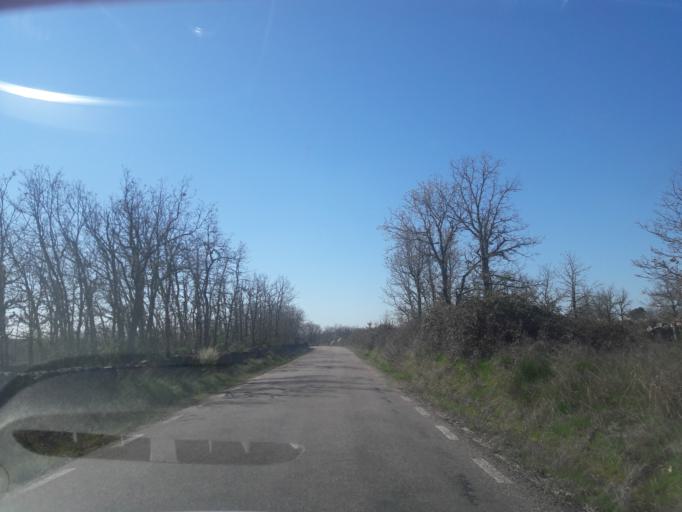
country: ES
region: Castille and Leon
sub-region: Provincia de Salamanca
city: Valsalabroso
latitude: 41.1176
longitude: -6.4834
